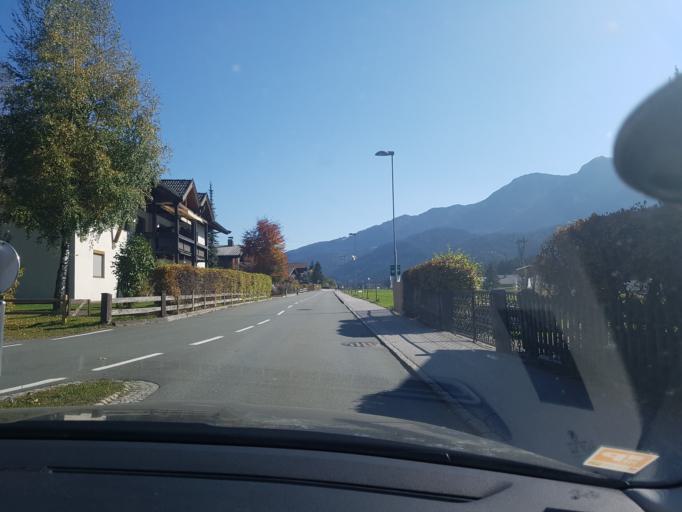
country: AT
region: Tyrol
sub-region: Politischer Bezirk Kitzbuhel
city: Hochfilzen
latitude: 47.4722
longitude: 12.6214
